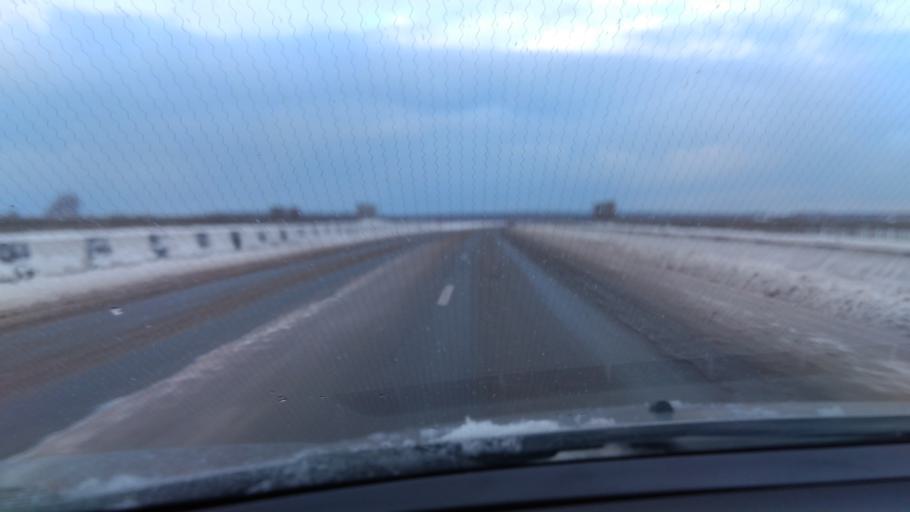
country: RU
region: Sverdlovsk
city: Nev'yansk
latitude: 57.5047
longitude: 60.1736
